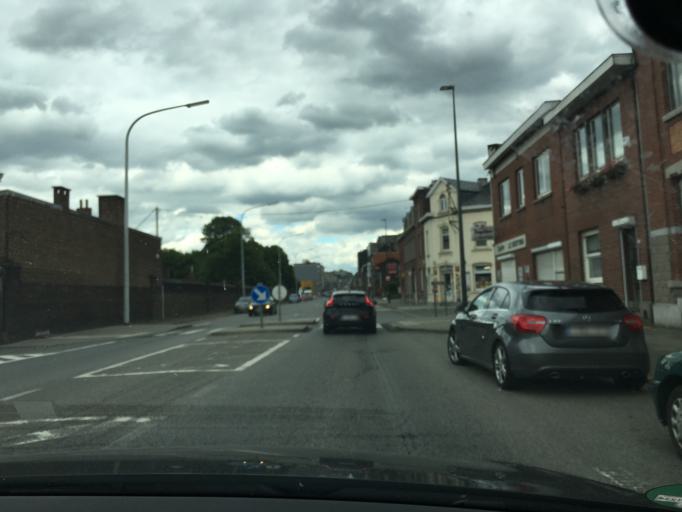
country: BE
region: Wallonia
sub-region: Province de Liege
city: Herstal
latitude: 50.6309
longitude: 5.6075
